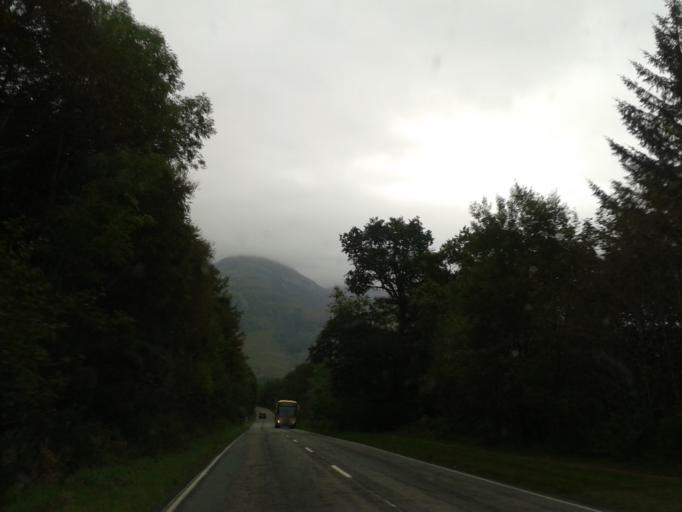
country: GB
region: Scotland
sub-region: Highland
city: Fort William
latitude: 57.2368
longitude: -5.4356
